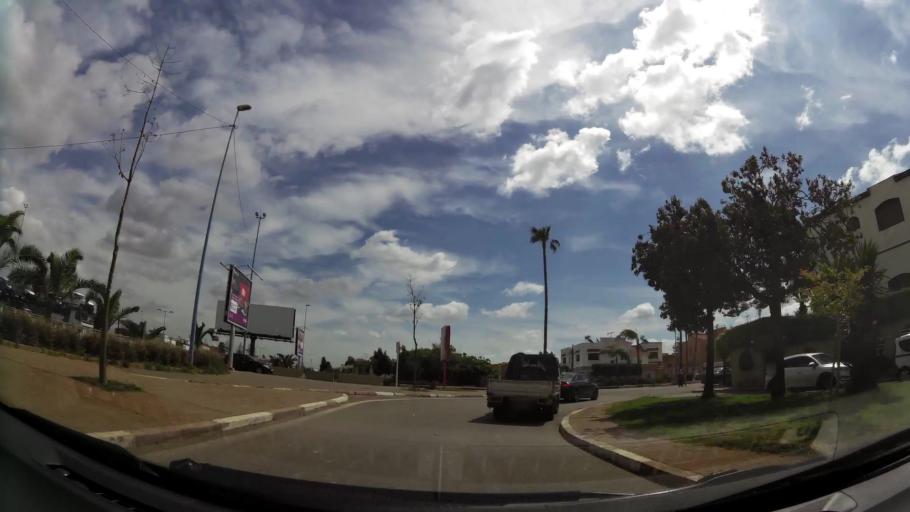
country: MA
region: Grand Casablanca
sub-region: Casablanca
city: Casablanca
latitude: 33.5530
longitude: -7.6238
